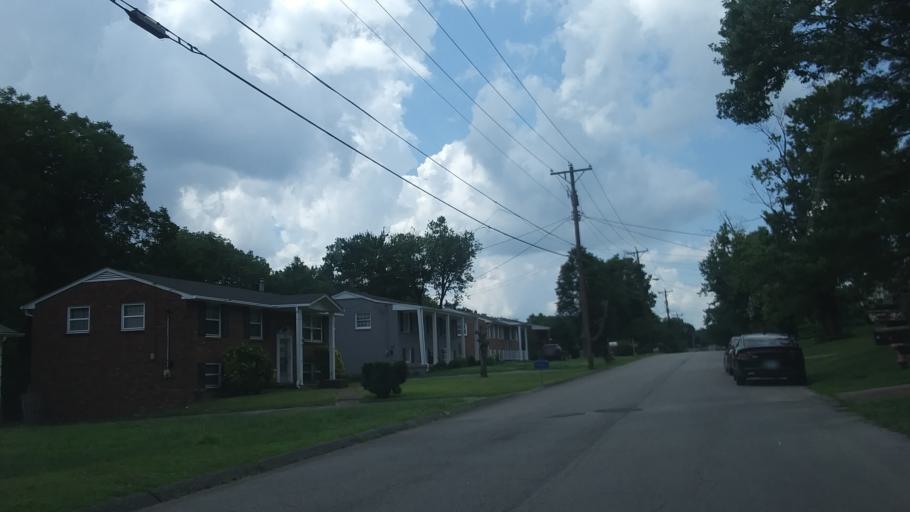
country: US
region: Tennessee
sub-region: Davidson County
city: Oak Hill
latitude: 36.0757
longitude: -86.7115
